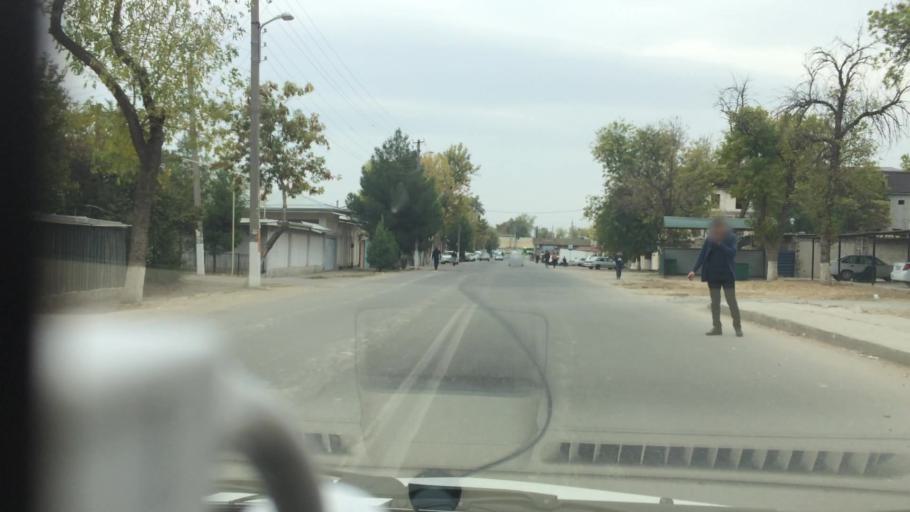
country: UZ
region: Toshkent Shahri
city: Tashkent
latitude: 41.2798
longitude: 69.2698
